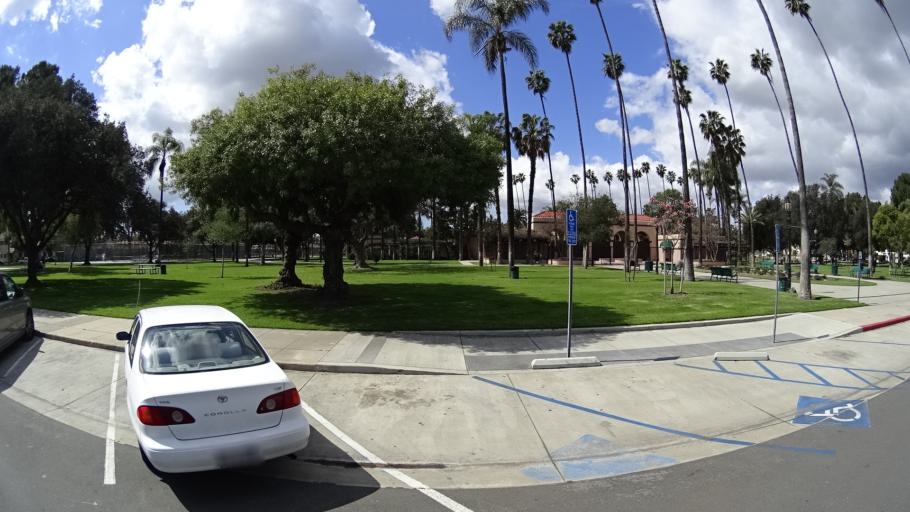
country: US
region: California
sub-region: Orange County
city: Anaheim
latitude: 33.8380
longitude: -117.9168
